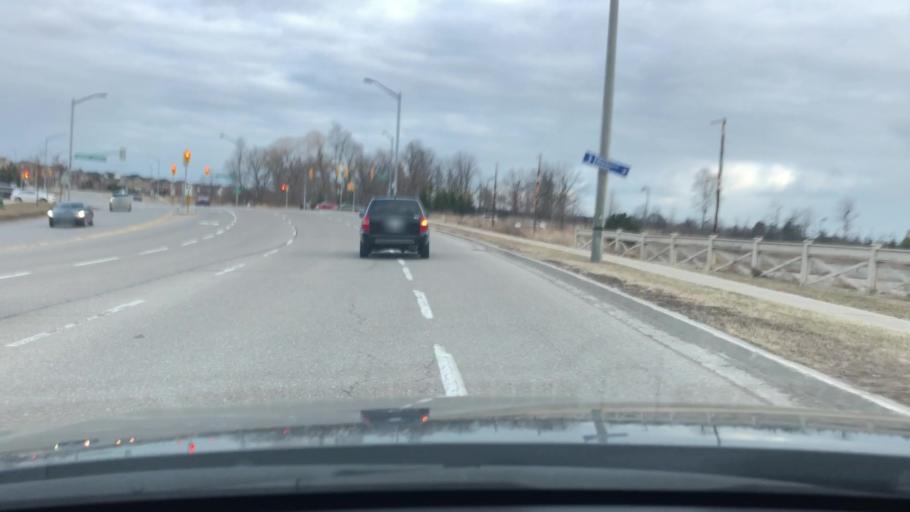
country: CA
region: Ontario
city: Markham
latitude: 43.8656
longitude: -79.2306
